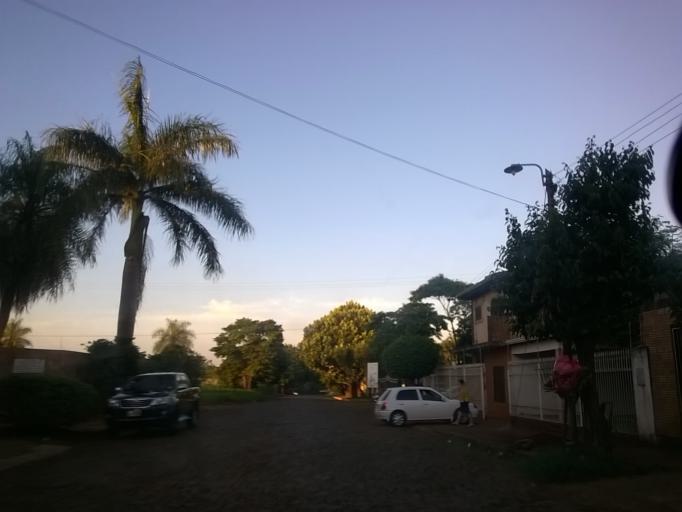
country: PY
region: Alto Parana
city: Ciudad del Este
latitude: -25.5112
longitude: -54.6540
